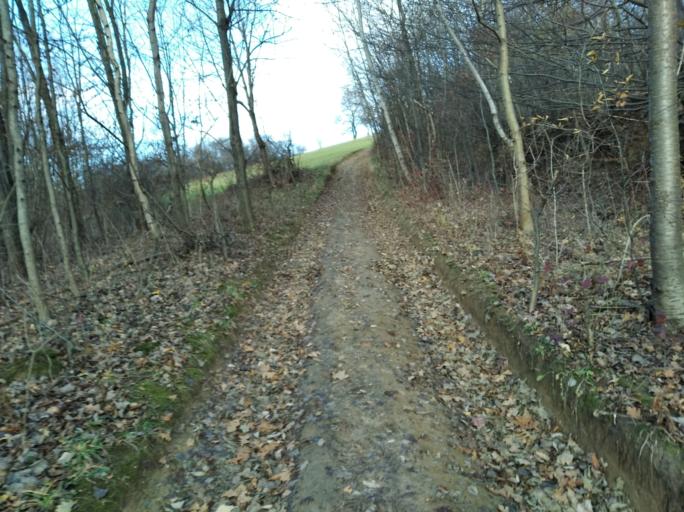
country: PL
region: Subcarpathian Voivodeship
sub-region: Powiat strzyzowski
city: Strzyzow
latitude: 49.8449
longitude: 21.8353
